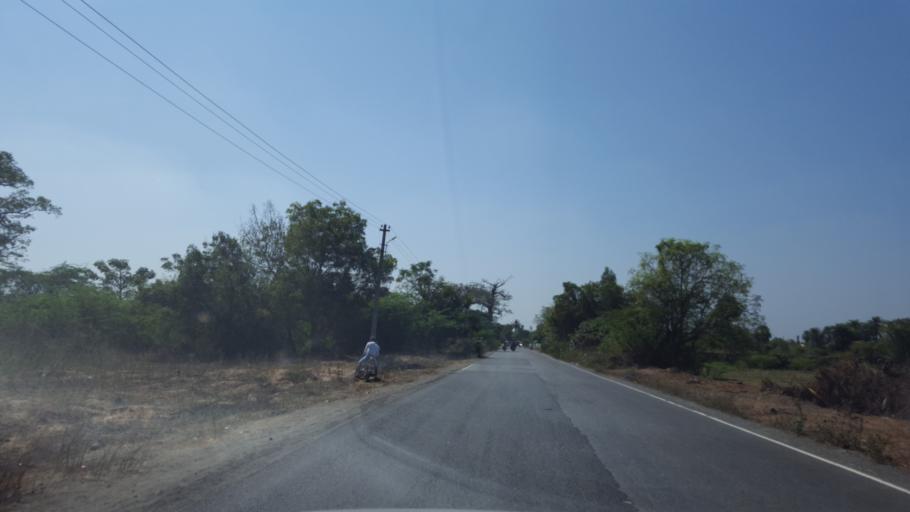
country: IN
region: Tamil Nadu
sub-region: Kancheepuram
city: Wallajahbad
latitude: 12.7852
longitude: 79.8343
